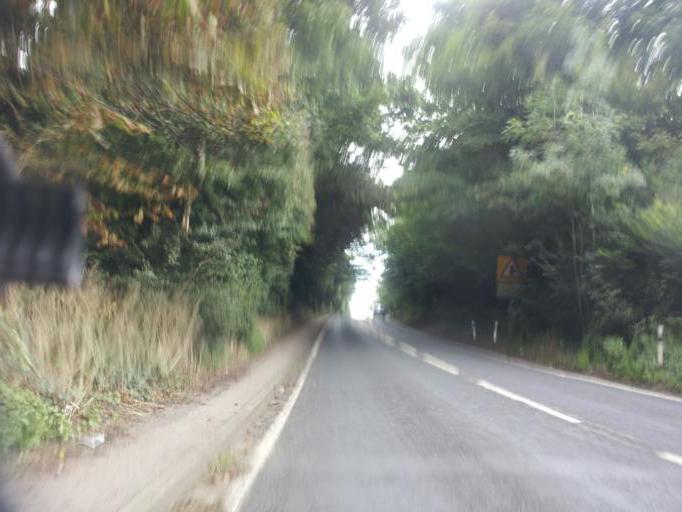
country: GB
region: England
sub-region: Kent
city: Newington
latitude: 51.3564
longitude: 0.6440
